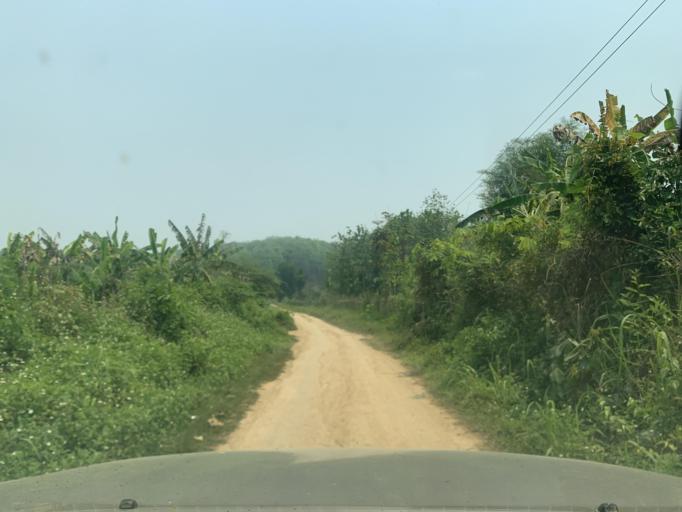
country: LA
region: Louangphabang
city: Xiang Ngeun
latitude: 19.8244
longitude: 102.2132
